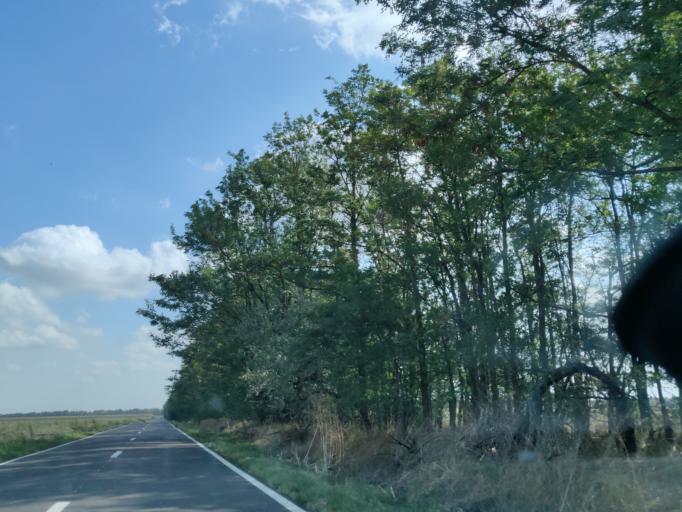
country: RO
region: Vrancea
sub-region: Comuna Ciorasti
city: Mihalceni
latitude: 45.4519
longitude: 27.3862
